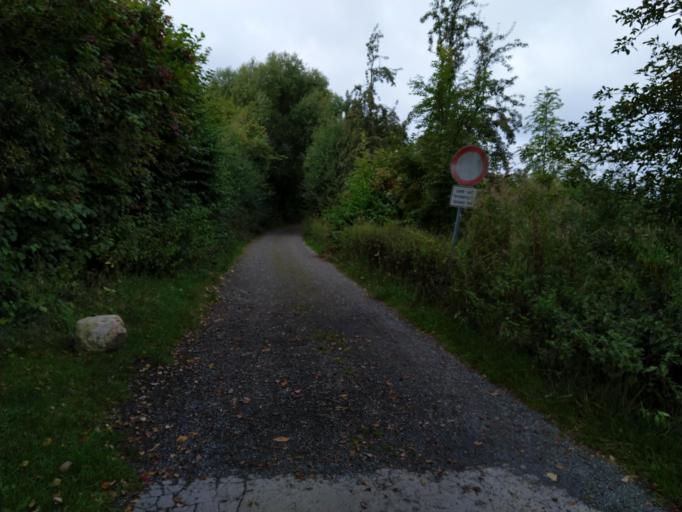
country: DE
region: North Rhine-Westphalia
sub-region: Regierungsbezirk Detmold
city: Bad Salzuflen
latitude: 52.0876
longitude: 8.8036
